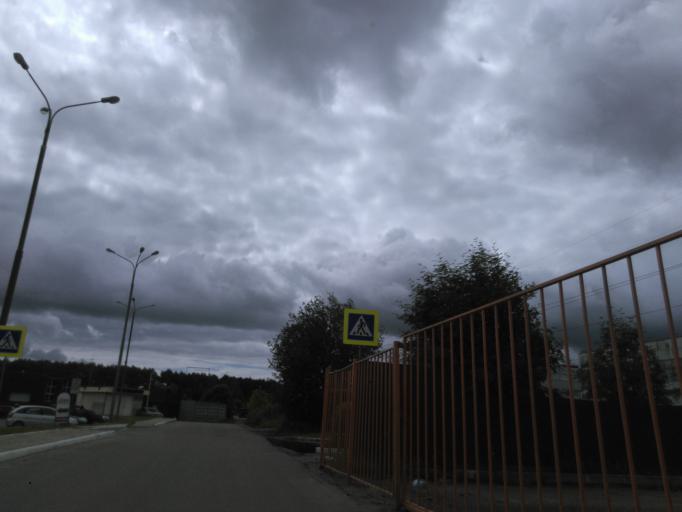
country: RU
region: Moskovskaya
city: Solnechnogorsk
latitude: 56.1978
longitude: 36.9564
